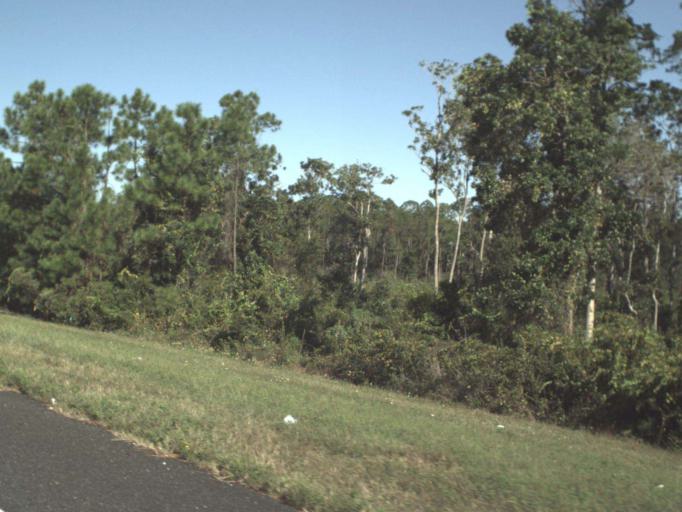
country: US
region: Florida
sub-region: Bay County
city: Panama City Beach
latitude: 30.2041
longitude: -85.8247
